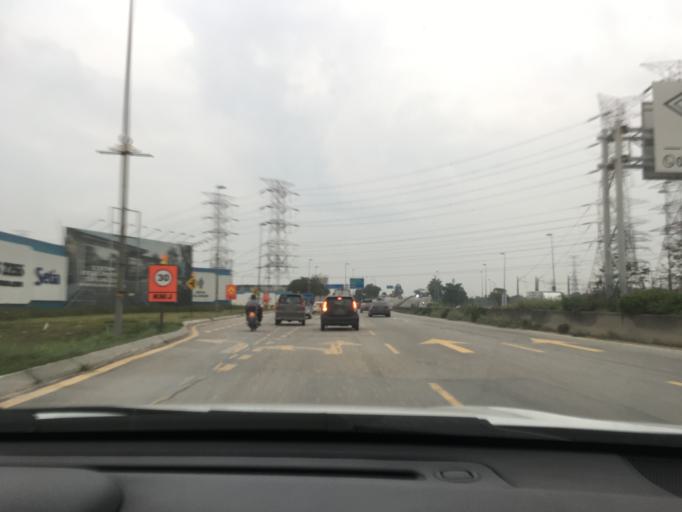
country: MY
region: Selangor
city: Klang
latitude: 3.1026
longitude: 101.4423
